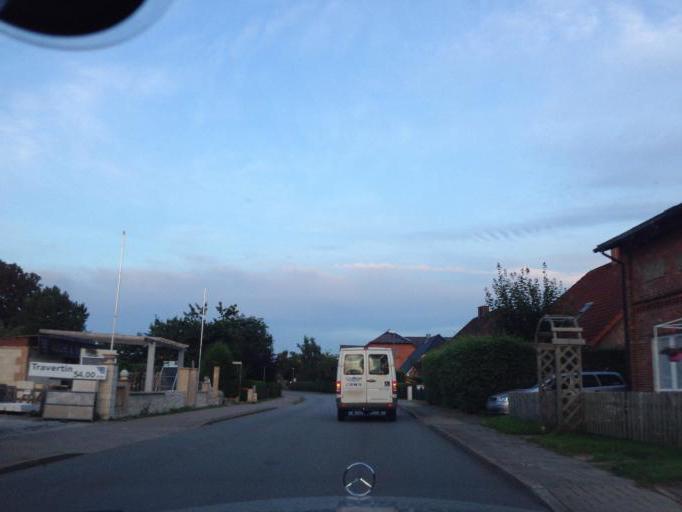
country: DE
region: Schleswig-Holstein
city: Hammoor
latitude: 53.7141
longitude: 10.3165
